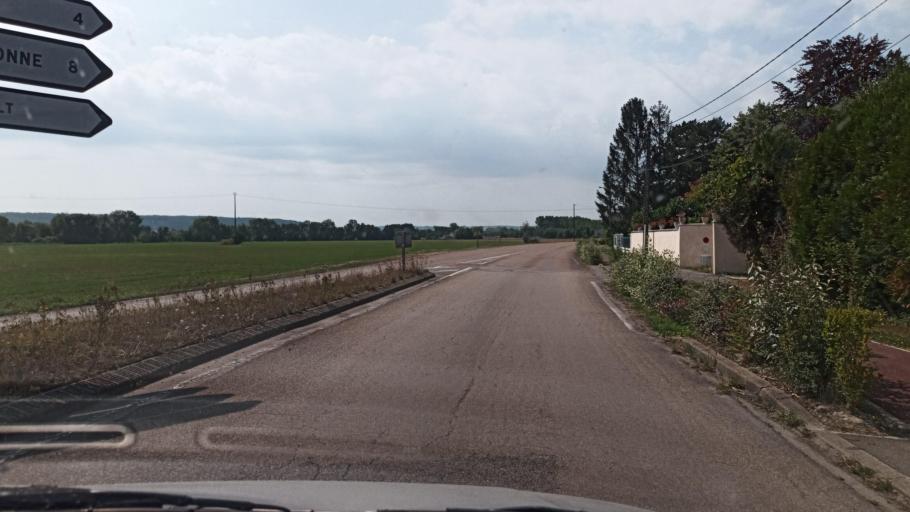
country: FR
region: Bourgogne
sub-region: Departement de l'Yonne
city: Veron
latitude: 48.1353
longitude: 3.2917
